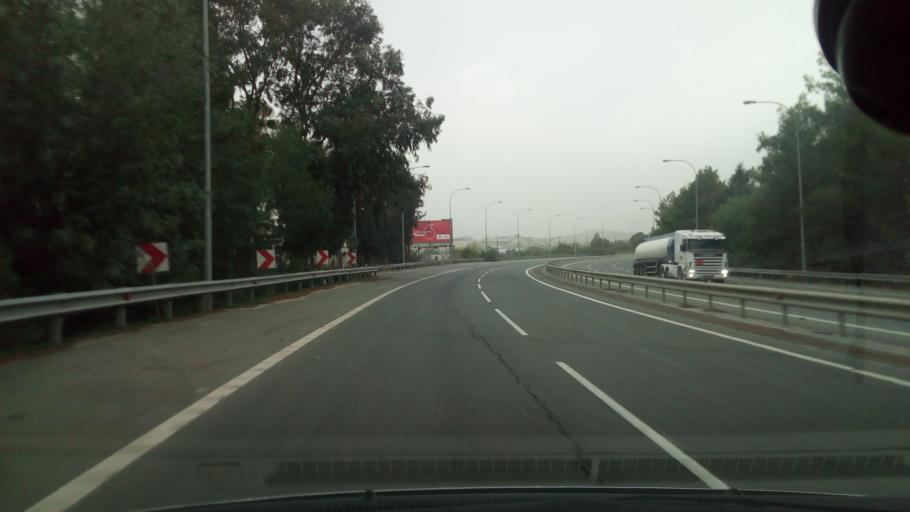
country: CY
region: Larnaka
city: Kofinou
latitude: 34.8309
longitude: 33.4014
